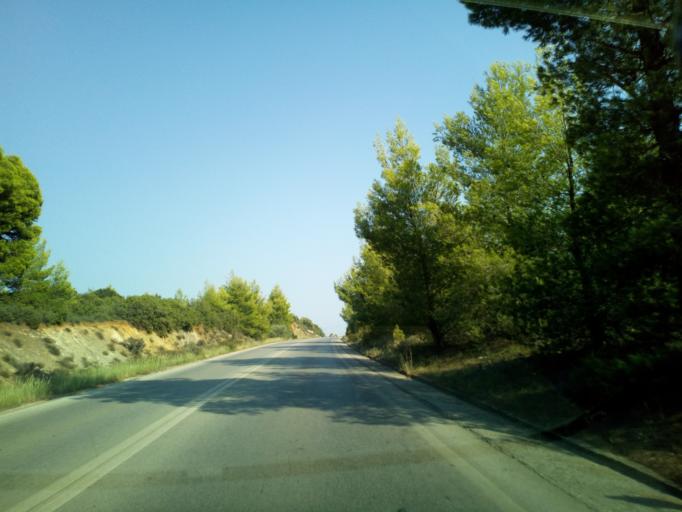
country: GR
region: Central Macedonia
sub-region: Nomos Chalkidikis
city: Ormylia
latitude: 40.2490
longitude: 23.5776
